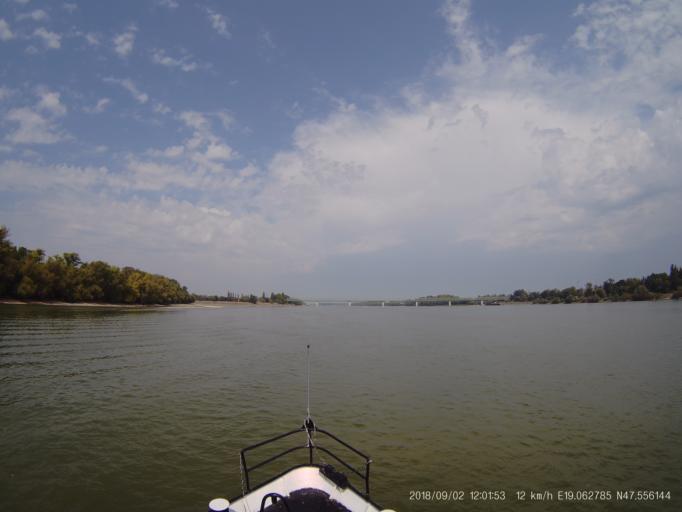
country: HU
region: Budapest
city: Budapest III. keruelet
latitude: 47.5587
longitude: 19.0633
